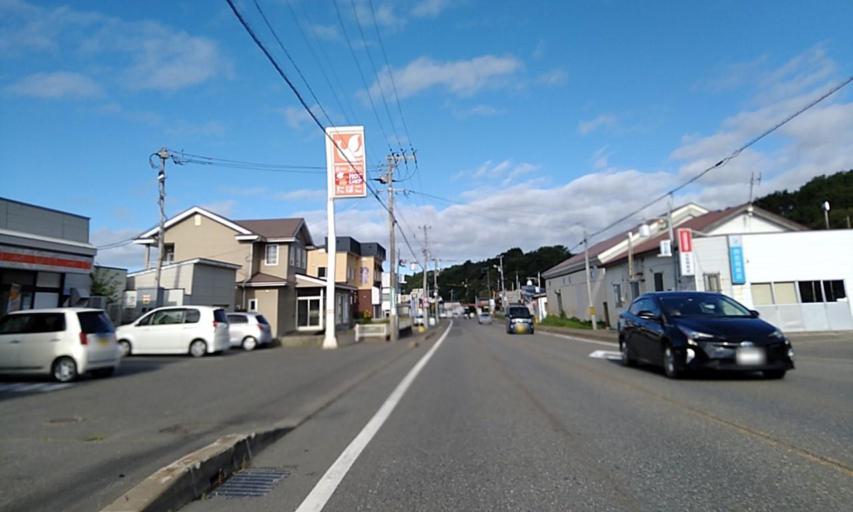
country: JP
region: Hokkaido
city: Shizunai-furukawacho
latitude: 42.2470
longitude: 142.5663
